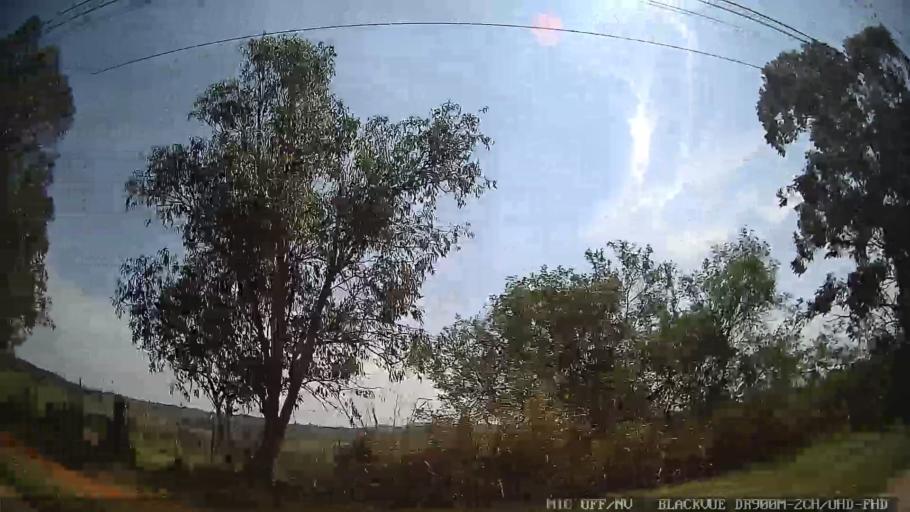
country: BR
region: Sao Paulo
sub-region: Cabreuva
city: Cabreuva
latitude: -23.2730
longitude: -47.0607
